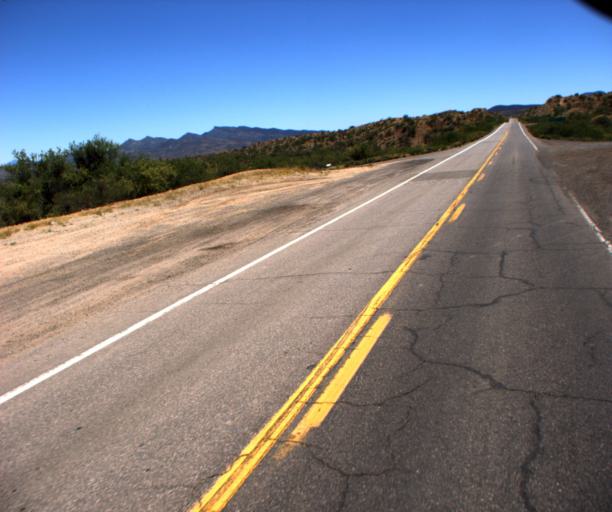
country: US
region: Arizona
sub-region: Gila County
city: Globe
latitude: 33.3721
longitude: -110.7381
